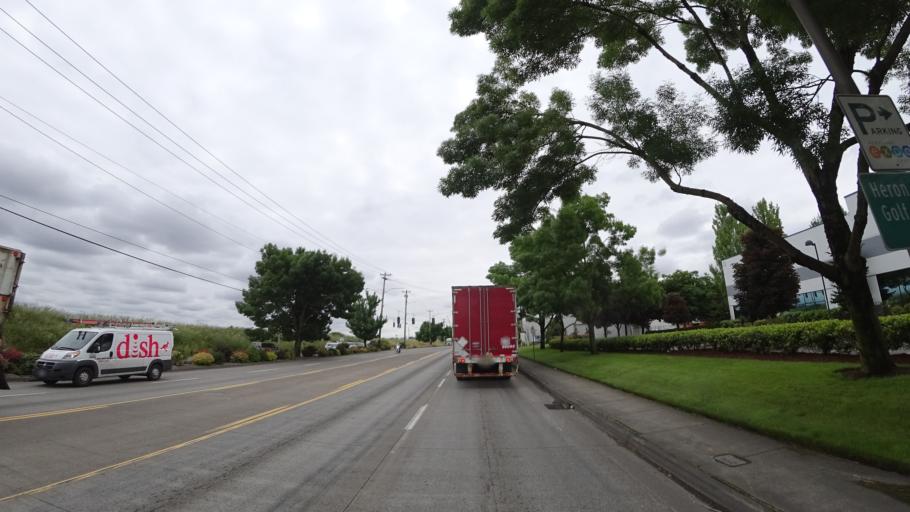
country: US
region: Washington
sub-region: Clark County
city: Vancouver
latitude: 45.6093
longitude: -122.6921
